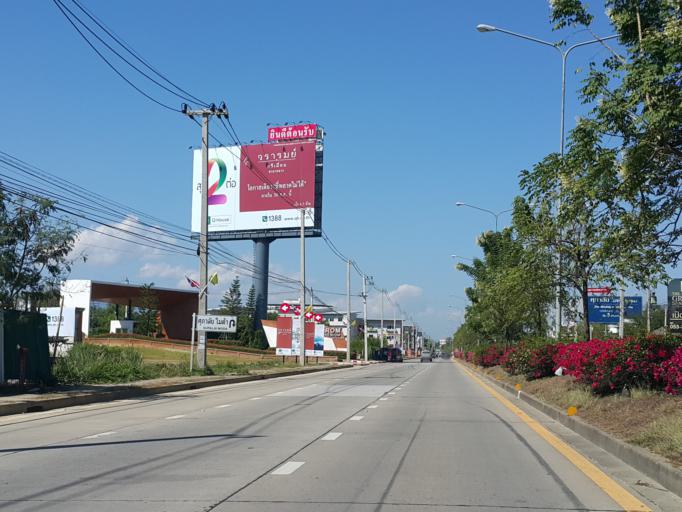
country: TH
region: Chiang Mai
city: San Sai
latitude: 18.8382
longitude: 99.0006
